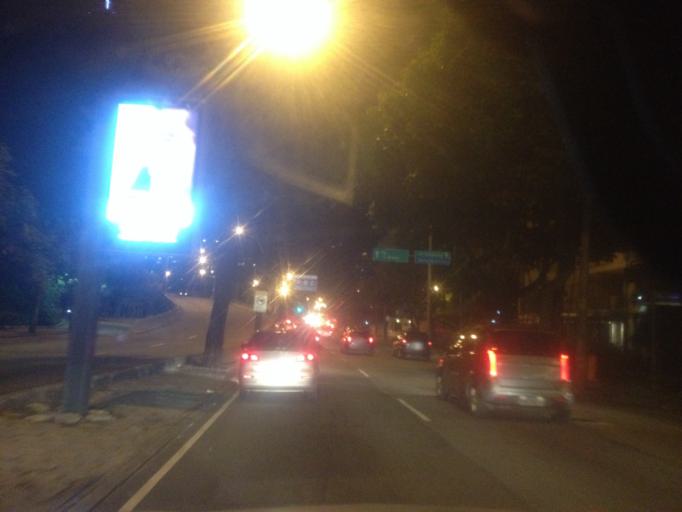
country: BR
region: Rio de Janeiro
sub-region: Rio De Janeiro
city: Rio de Janeiro
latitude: -22.9643
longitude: -43.2037
